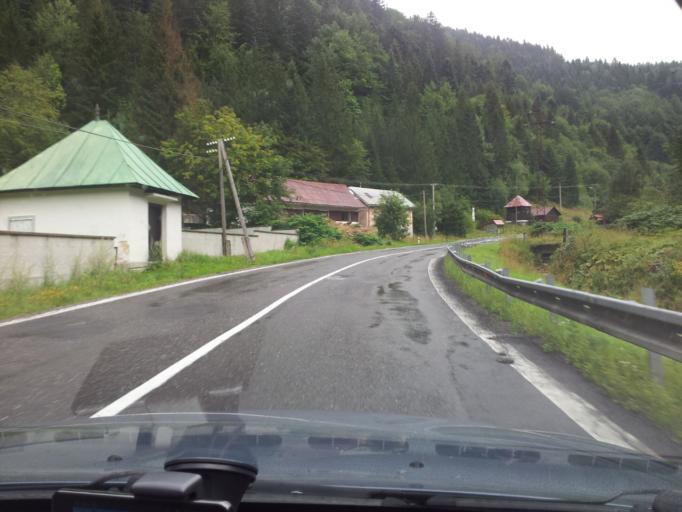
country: SK
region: Banskobystricky
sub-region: Okres Banska Bystrica
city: Brezno
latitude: 48.8907
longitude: 19.6898
